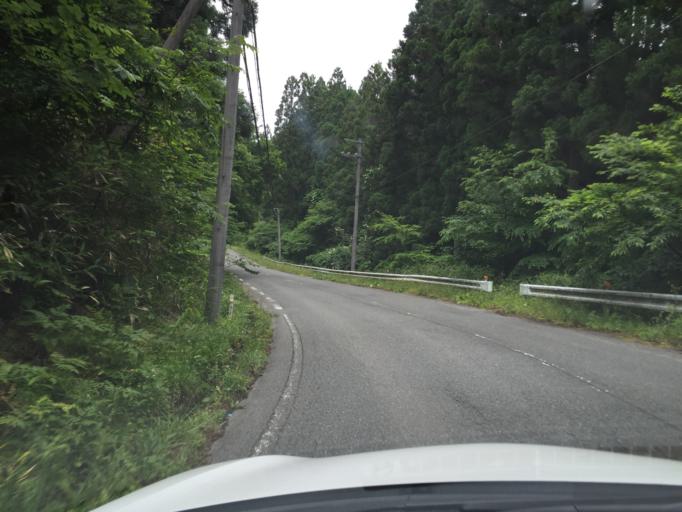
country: JP
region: Fukushima
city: Iwaki
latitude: 37.1697
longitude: 140.7110
